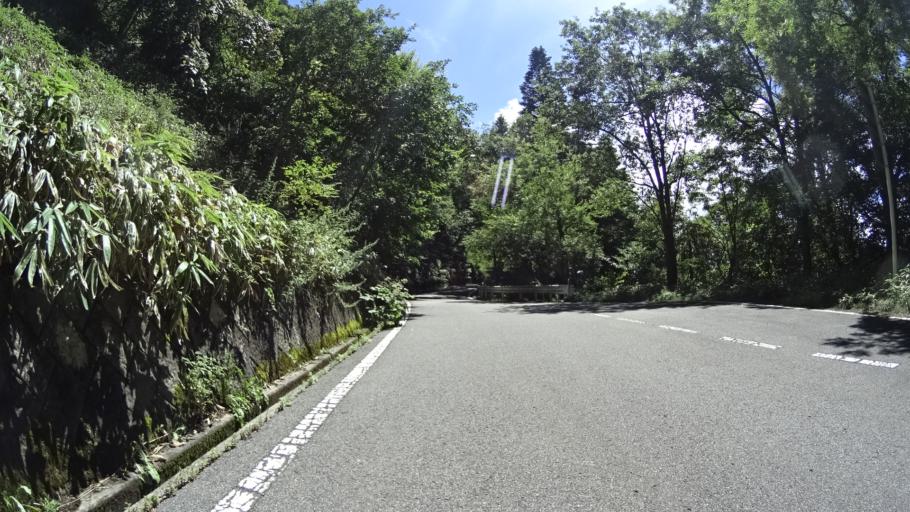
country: JP
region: Yamanashi
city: Enzan
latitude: 35.7328
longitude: 138.8370
